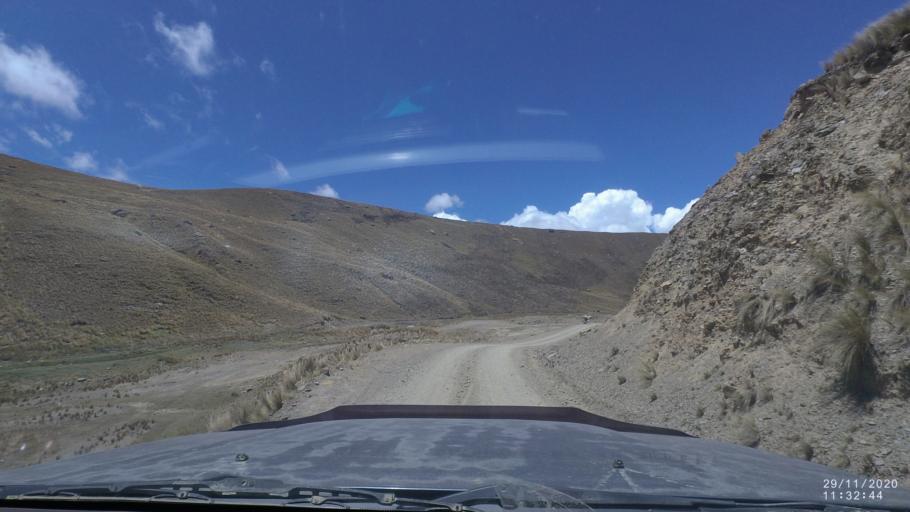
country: BO
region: Cochabamba
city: Cochabamba
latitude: -17.1863
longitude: -66.2103
